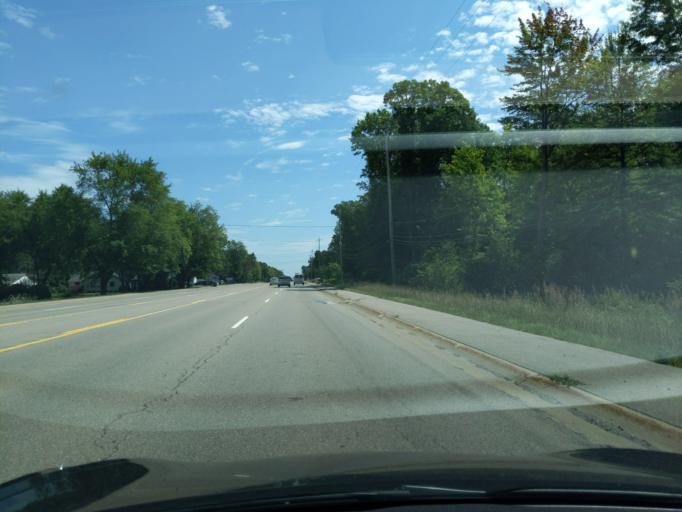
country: US
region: Michigan
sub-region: Midland County
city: Midland
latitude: 43.6124
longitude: -84.3645
